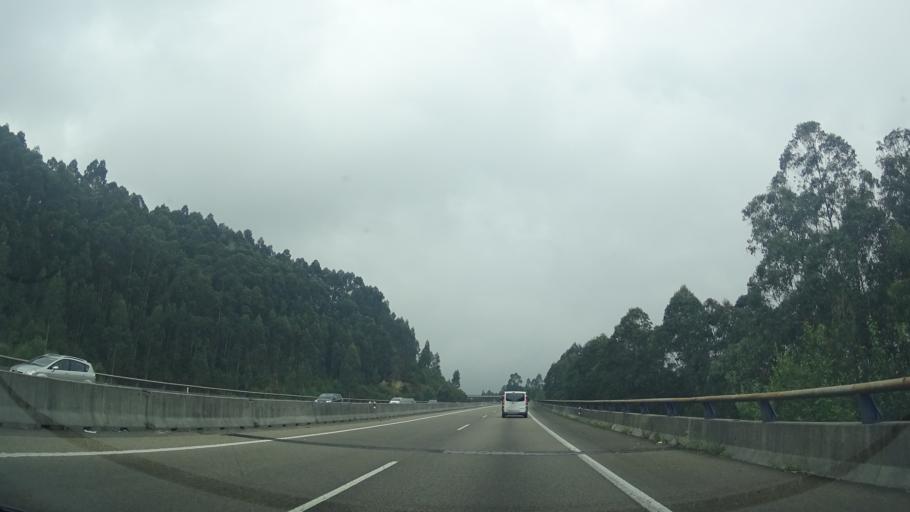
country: ES
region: Asturias
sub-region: Province of Asturias
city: Arriba
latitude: 43.5029
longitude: -5.5422
